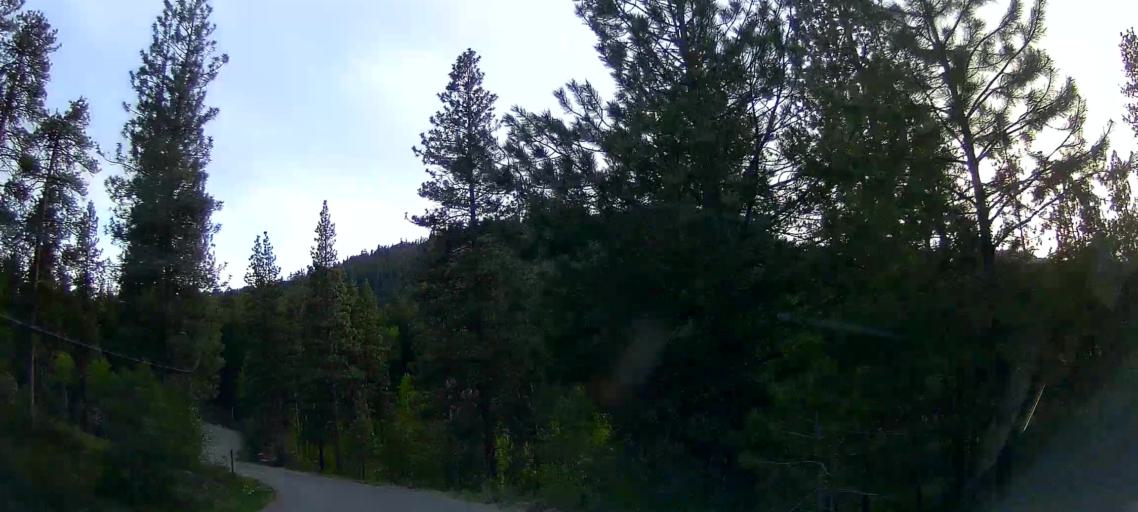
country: US
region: Washington
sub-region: Chelan County
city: Granite Falls
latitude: 48.4656
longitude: -120.2604
